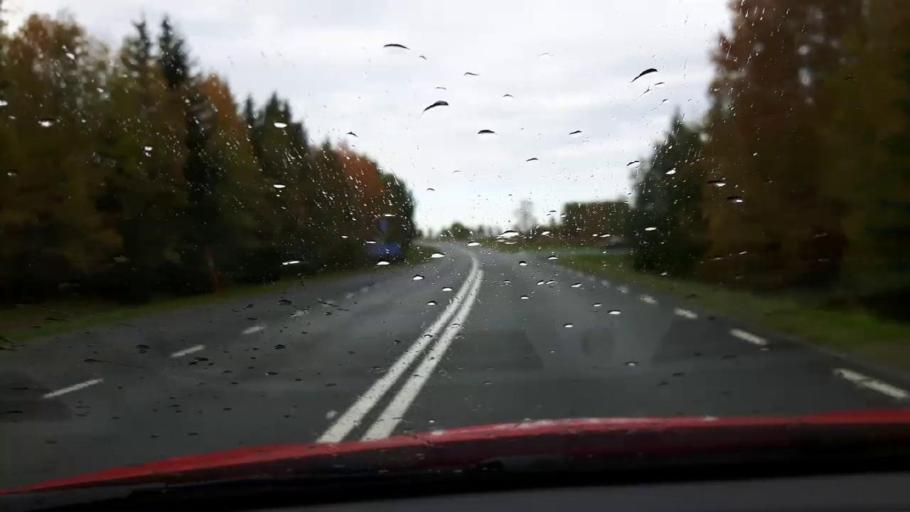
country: SE
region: Jaemtland
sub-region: Krokoms Kommun
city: Krokom
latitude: 63.1246
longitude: 14.2937
